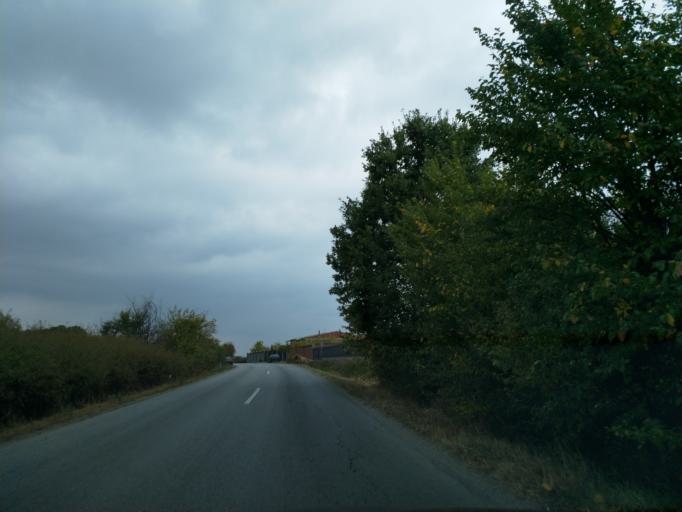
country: RS
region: Central Serbia
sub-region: Pomoravski Okrug
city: Jagodina
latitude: 44.0158
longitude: 21.1991
